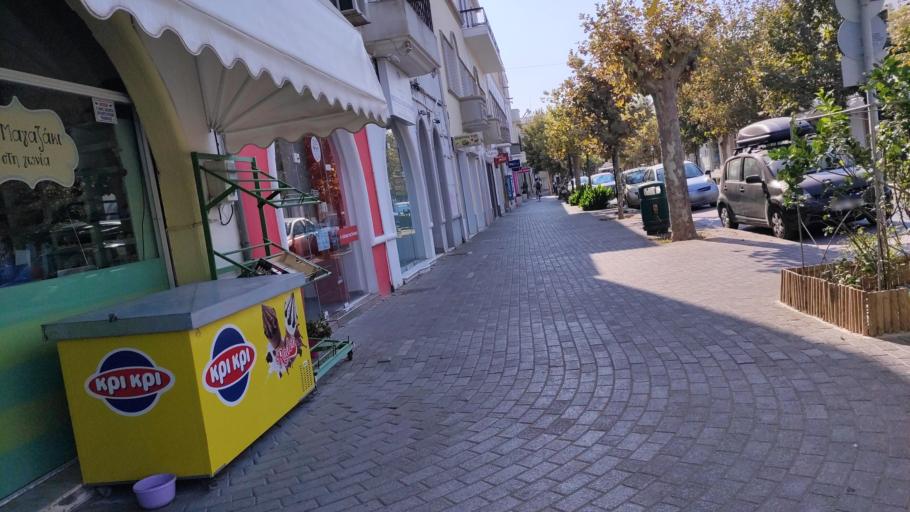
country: GR
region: South Aegean
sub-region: Nomos Dodekanisou
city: Kos
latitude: 36.8928
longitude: 27.2911
